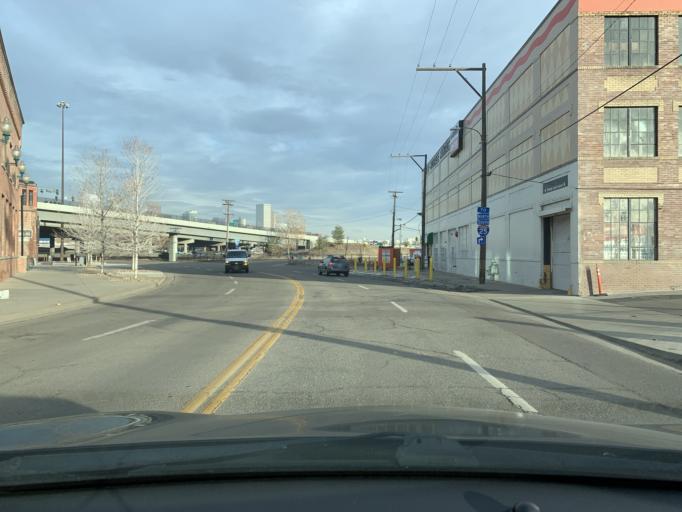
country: US
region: Colorado
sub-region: Denver County
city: Denver
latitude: 39.7396
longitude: -105.0168
